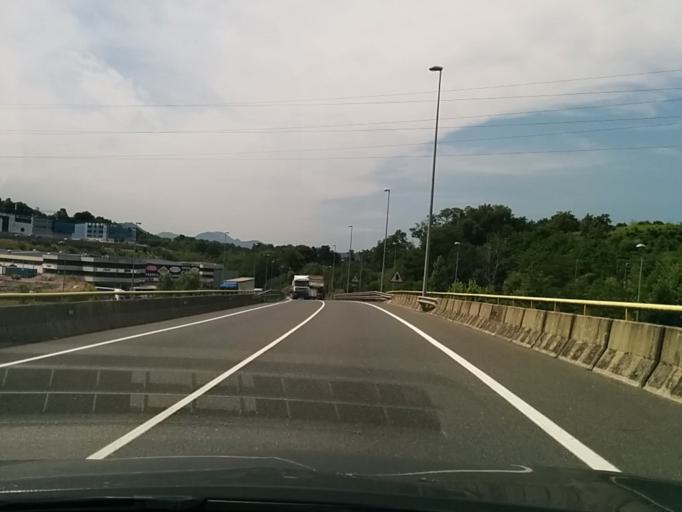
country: ES
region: Basque Country
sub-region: Provincia de Guipuzcoa
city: Lezo
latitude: 43.3204
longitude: -1.8673
